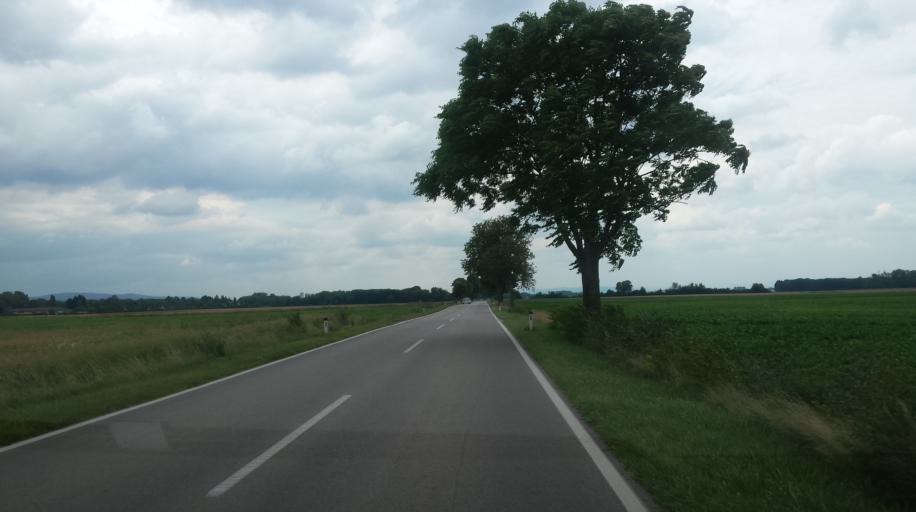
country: AT
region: Lower Austria
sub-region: Politischer Bezirk Baden
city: Mitterndorf an der Fischa
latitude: 47.9884
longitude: 16.4392
